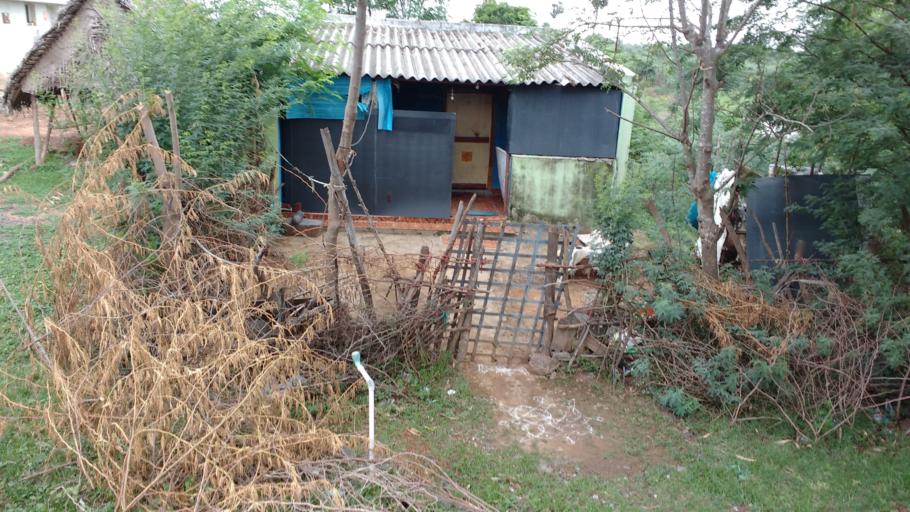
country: IN
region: Tamil Nadu
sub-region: Kancheepuram
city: Sriperumbudur
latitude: 12.9510
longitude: 80.0031
